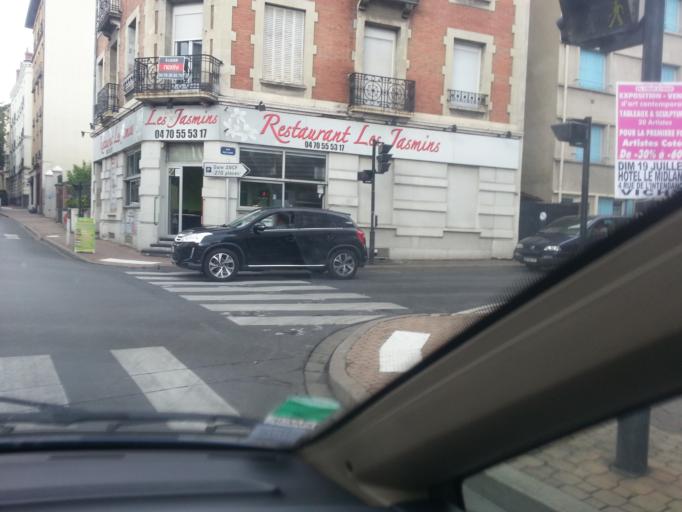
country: FR
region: Auvergne
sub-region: Departement de l'Allier
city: Vichy
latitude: 46.1244
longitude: 3.4296
